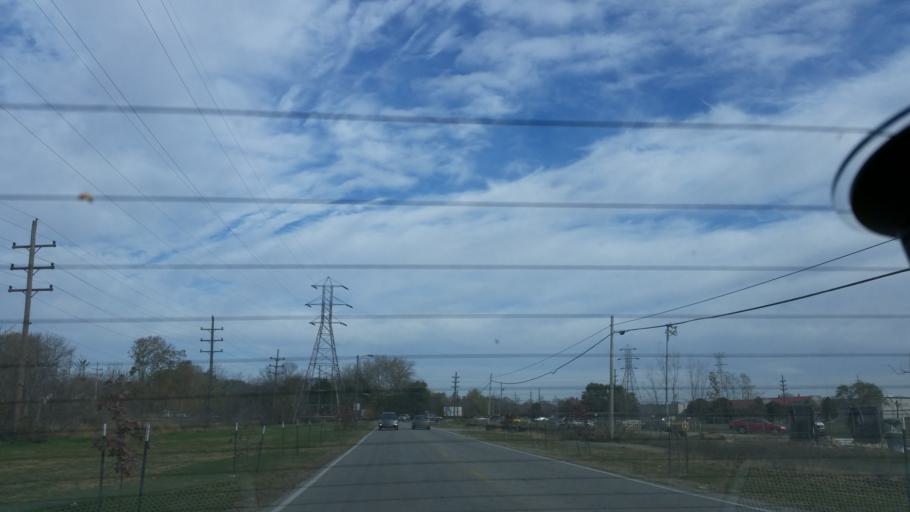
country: US
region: Indiana
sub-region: Howard County
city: Kokomo
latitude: 40.4749
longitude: -86.1490
